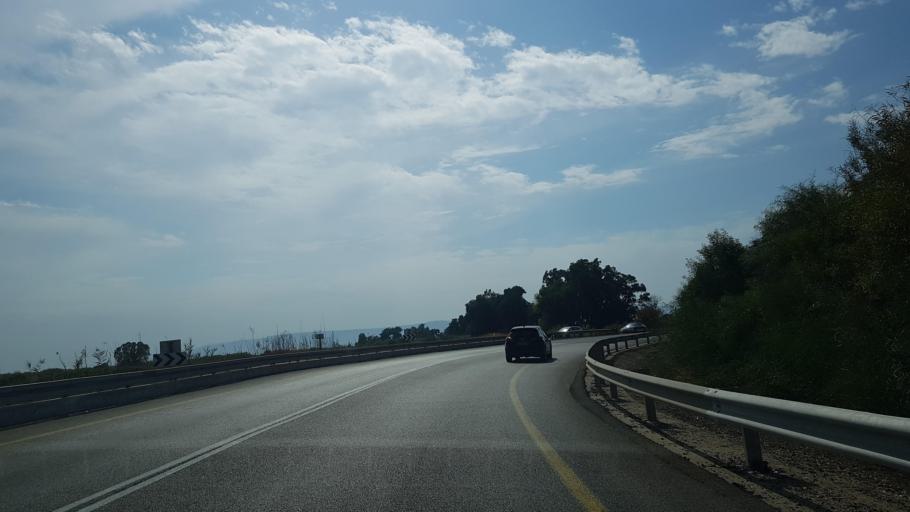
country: SY
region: Quneitra
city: Al Butayhah
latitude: 32.9028
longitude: 35.6169
